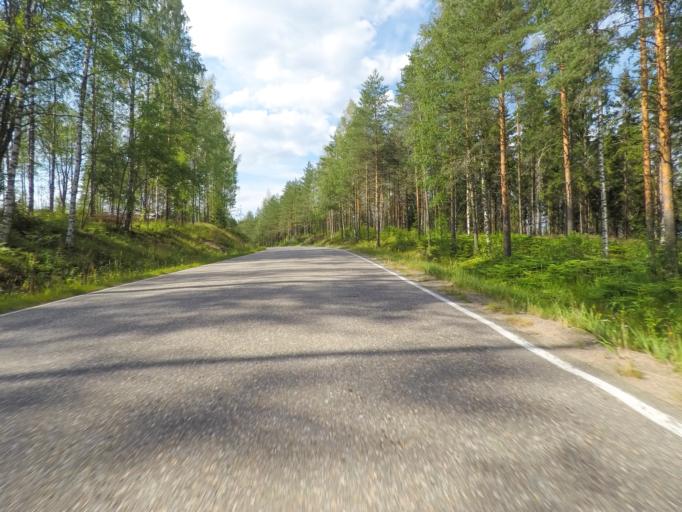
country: FI
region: Southern Savonia
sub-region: Mikkeli
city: Puumala
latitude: 61.6842
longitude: 28.2296
